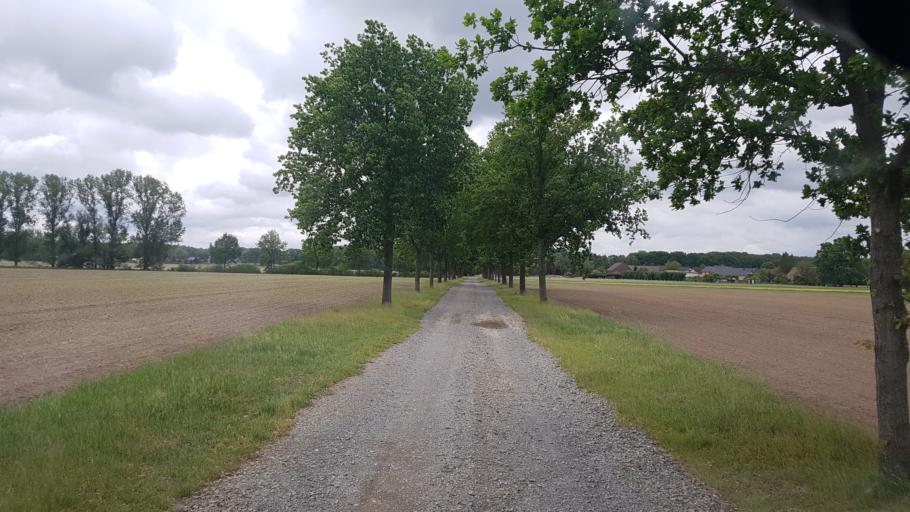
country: DE
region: Brandenburg
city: Schonewalde
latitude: 51.7065
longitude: 13.6029
